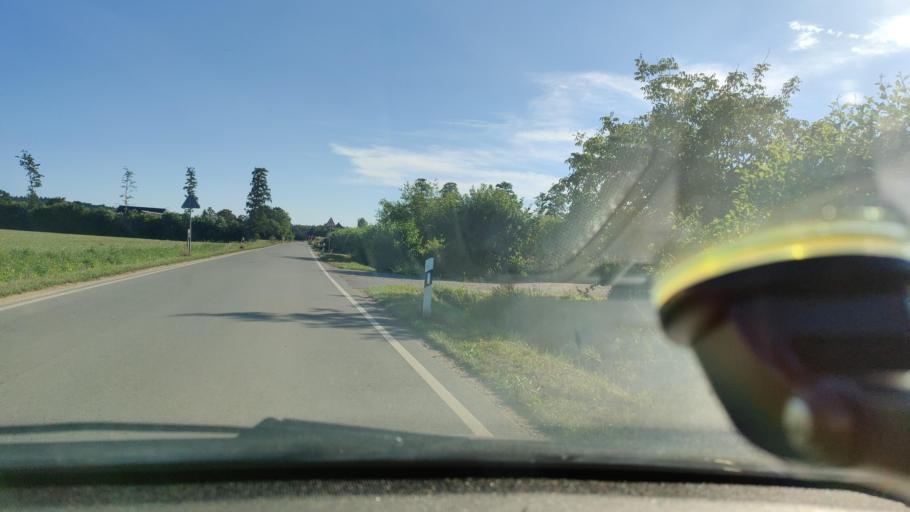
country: DE
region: North Rhine-Westphalia
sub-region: Regierungsbezirk Dusseldorf
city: Emmerich
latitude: 51.7745
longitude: 6.2139
